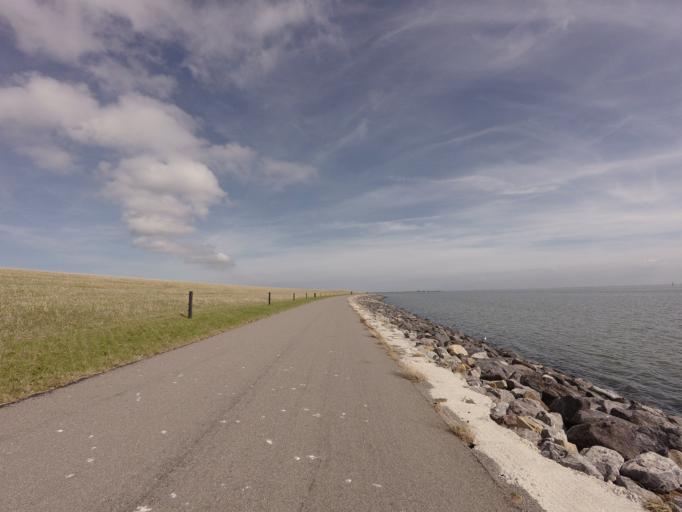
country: NL
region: Friesland
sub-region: Gemeente Ameland
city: Nes
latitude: 53.4411
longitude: 5.7492
